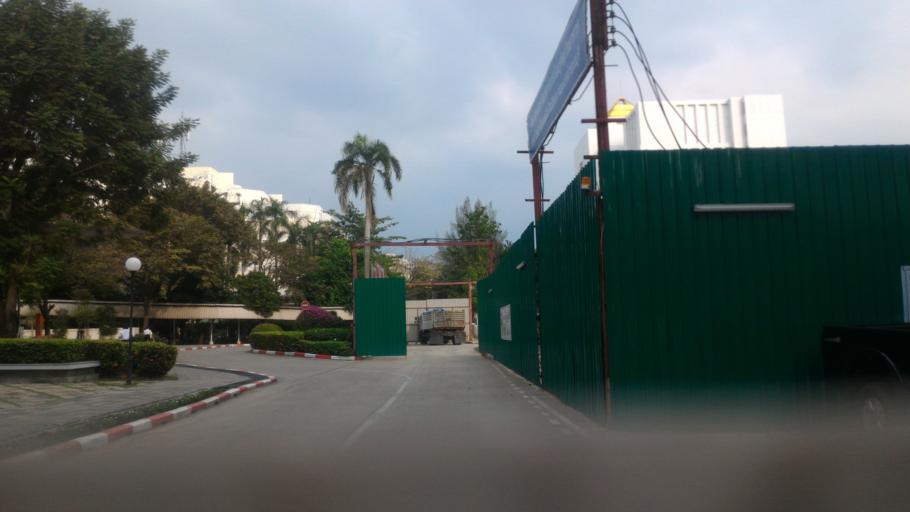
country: TH
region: Bangkok
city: Chom Thong
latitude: 13.6523
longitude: 100.4936
